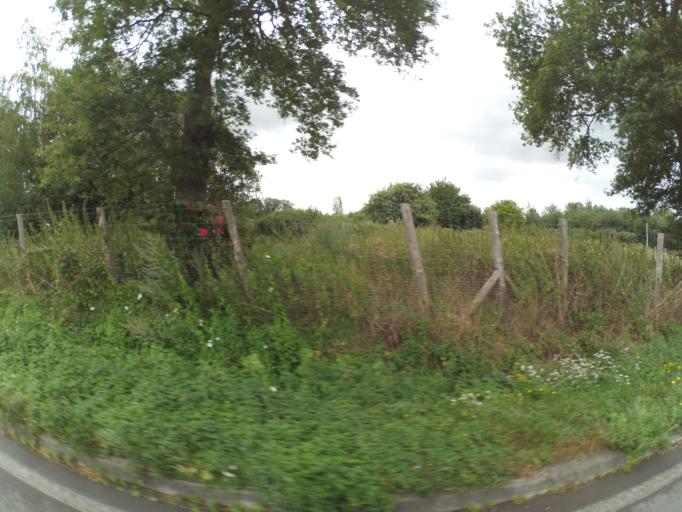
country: FR
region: Pays de la Loire
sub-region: Departement de Maine-et-Loire
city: Villedieu-la-Blouere
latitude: 47.1319
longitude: -1.0826
